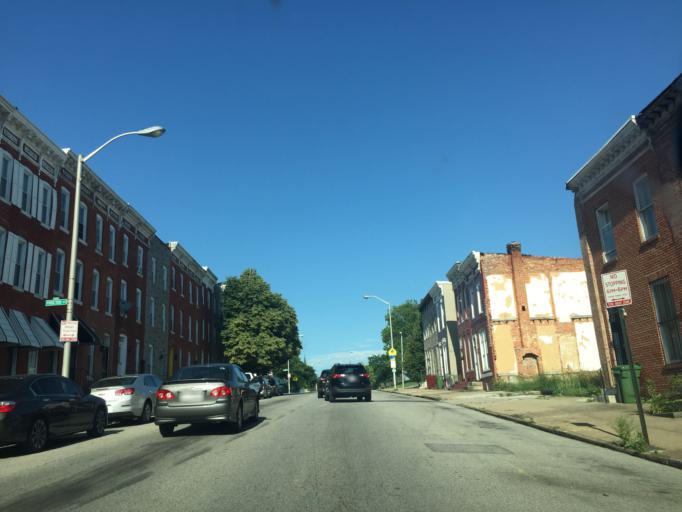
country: US
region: Maryland
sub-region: City of Baltimore
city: Baltimore
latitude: 39.3038
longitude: -76.6076
